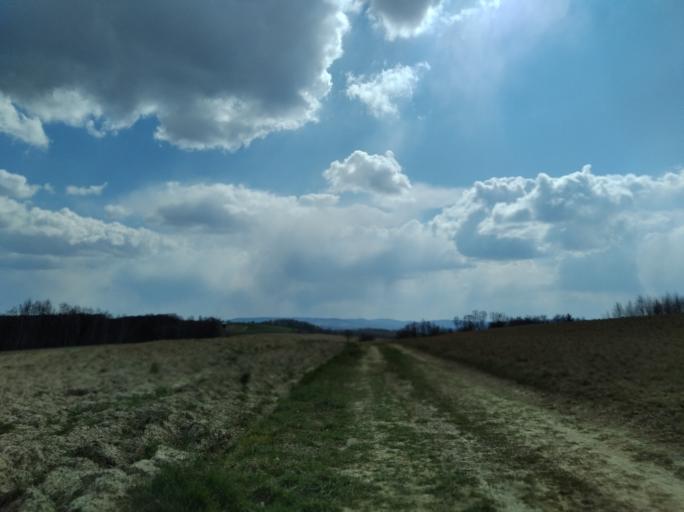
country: PL
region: Subcarpathian Voivodeship
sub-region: Powiat strzyzowski
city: Strzyzow
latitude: 49.9187
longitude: 21.7439
